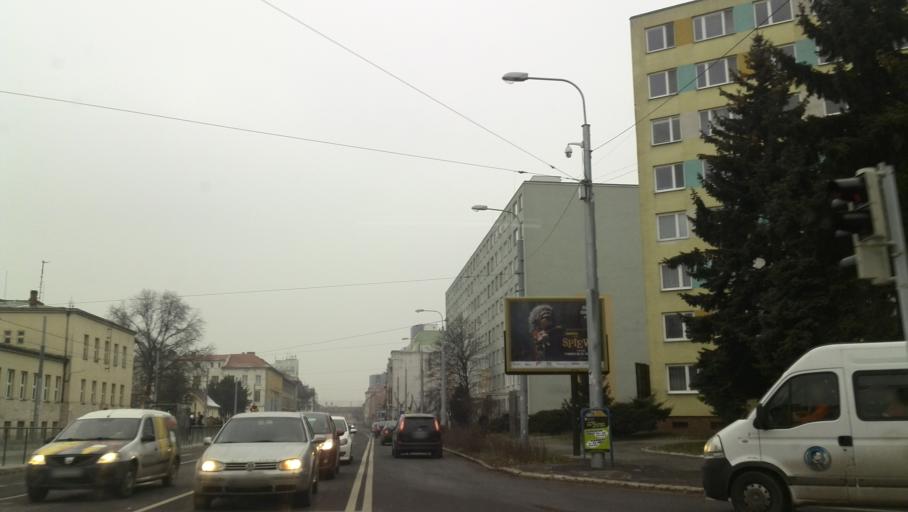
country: SK
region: Kosicky
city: Kosice
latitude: 48.7219
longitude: 21.2489
